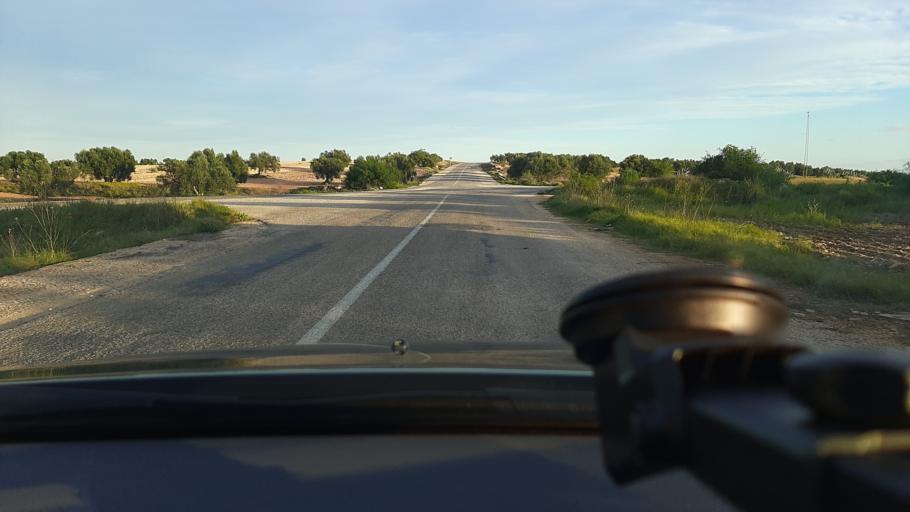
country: TN
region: Safaqis
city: Sfax
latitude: 34.9563
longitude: 10.5448
